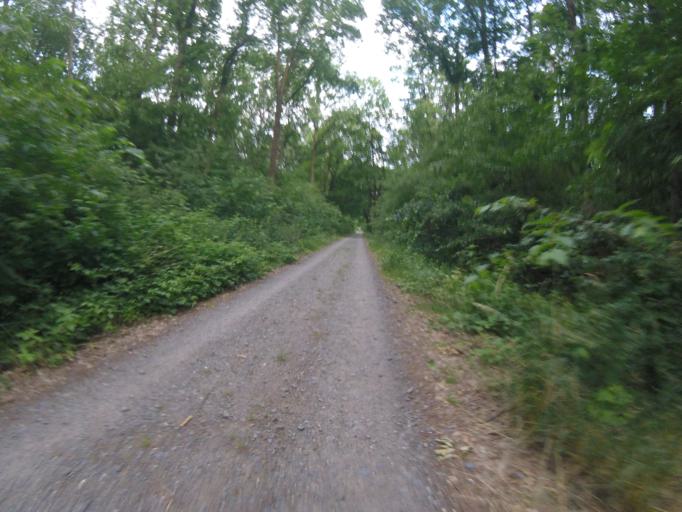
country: DE
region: Brandenburg
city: Konigs Wusterhausen
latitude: 52.3066
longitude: 13.6088
